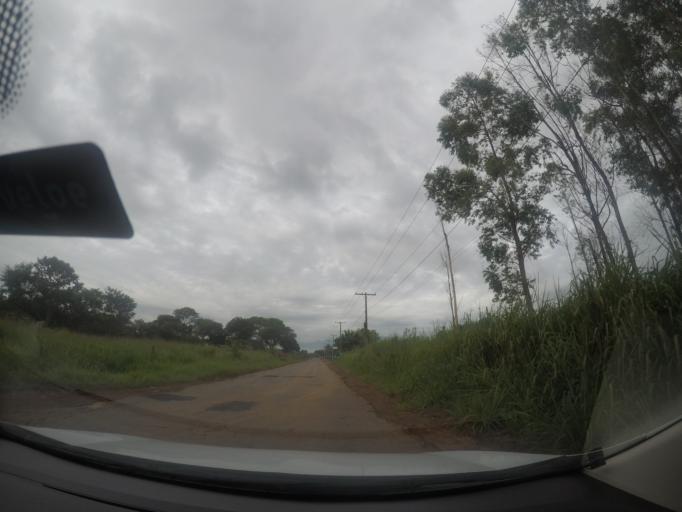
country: BR
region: Goias
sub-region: Goiania
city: Goiania
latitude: -16.6380
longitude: -49.3365
